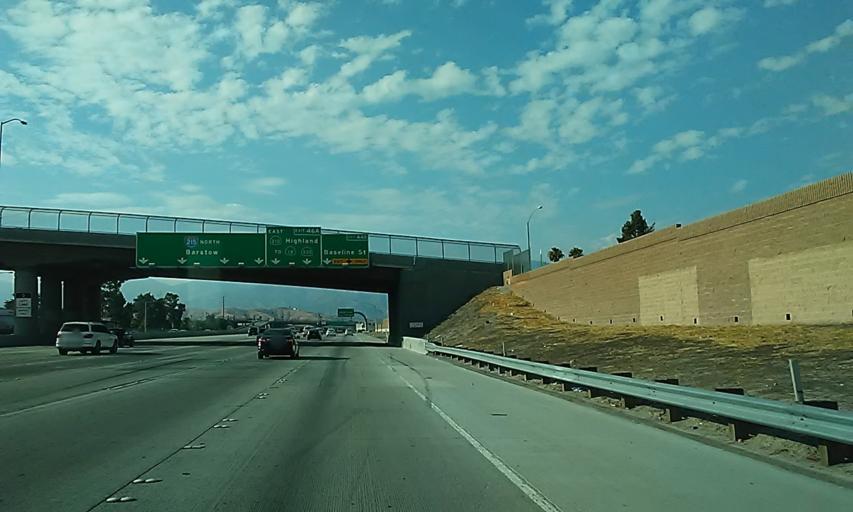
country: US
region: California
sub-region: San Bernardino County
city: San Bernardino
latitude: 34.1151
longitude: -117.3023
